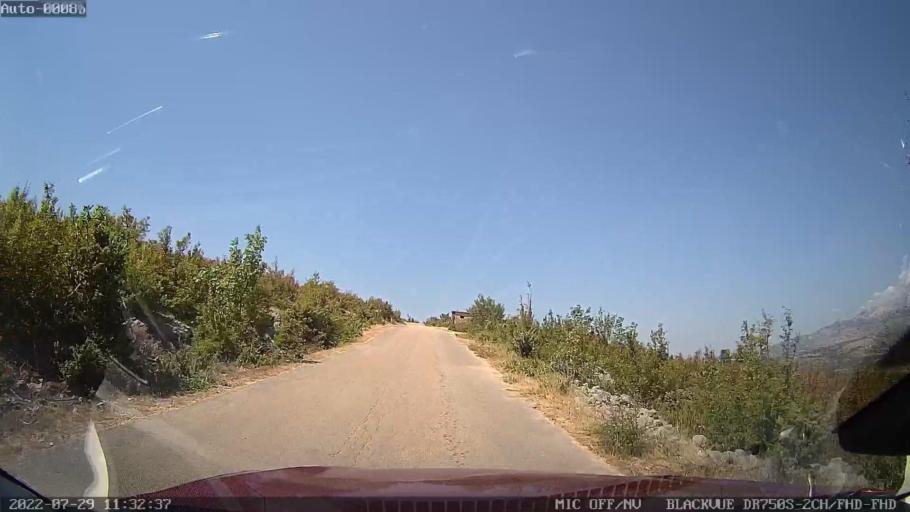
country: HR
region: Zadarska
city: Obrovac
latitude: 44.1910
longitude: 15.7366
